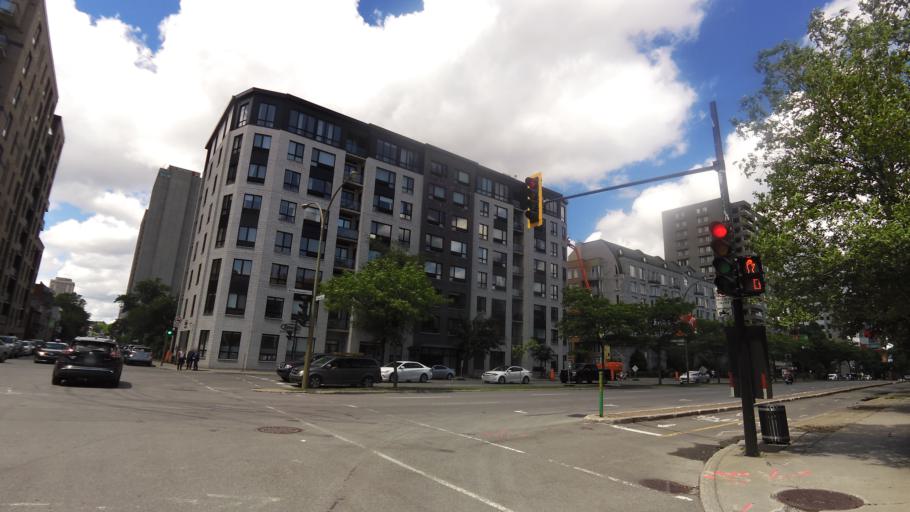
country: CA
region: Quebec
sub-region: Montreal
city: Montreal
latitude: 45.5143
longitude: -73.5564
